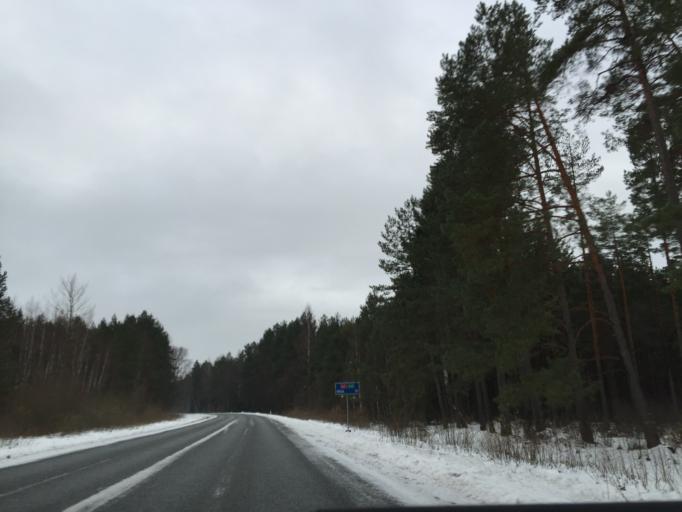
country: LV
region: Saulkrastu
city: Saulkrasti
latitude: 57.2157
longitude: 24.3839
